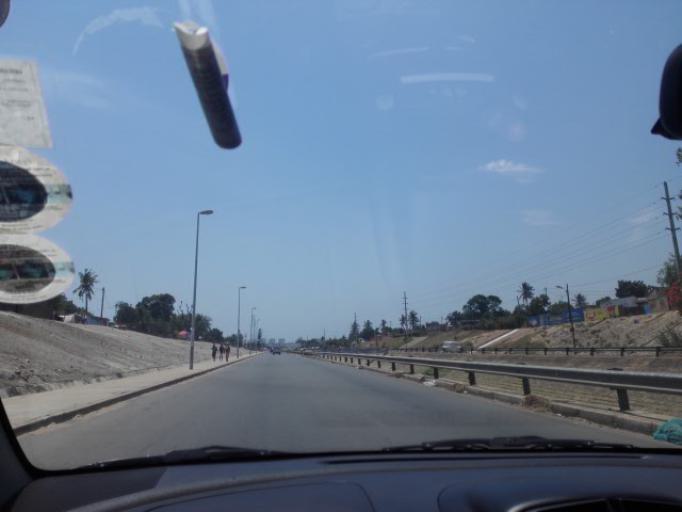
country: MZ
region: Maputo City
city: Maputo
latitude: -25.9347
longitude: 32.5631
